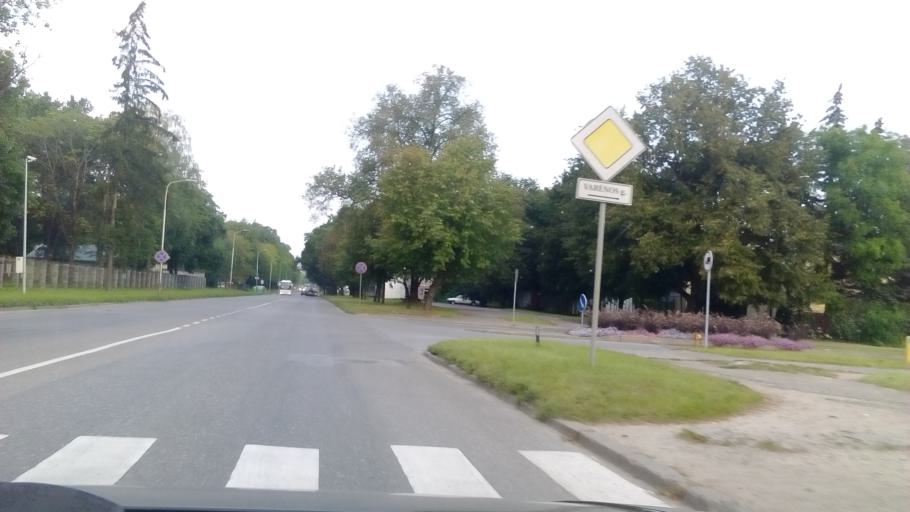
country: LT
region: Alytaus apskritis
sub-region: Alytus
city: Alytus
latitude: 54.3824
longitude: 24.0550
